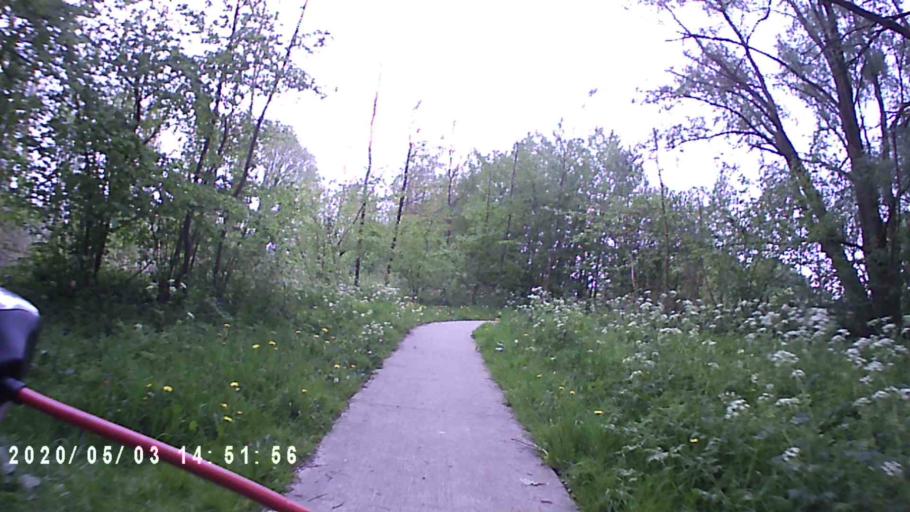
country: NL
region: Groningen
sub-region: Gemeente Zuidhorn
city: Oldehove
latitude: 53.3615
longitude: 6.4220
